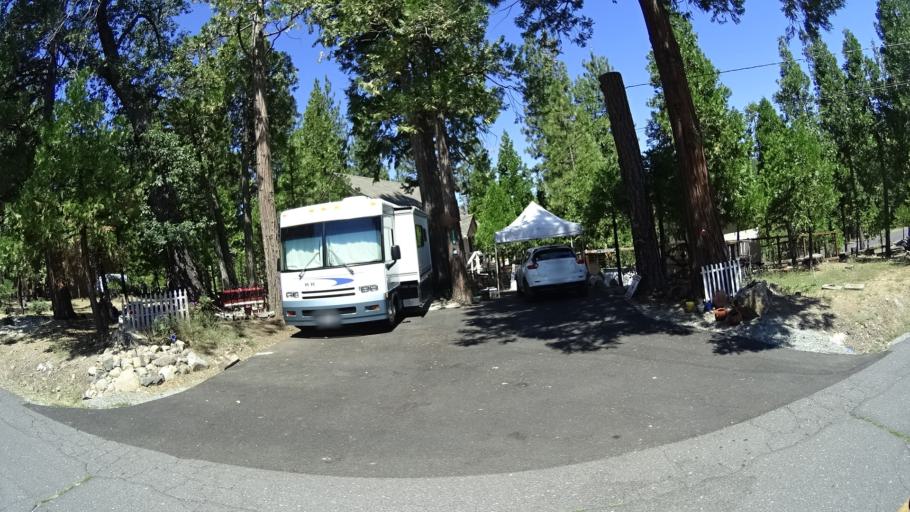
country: US
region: California
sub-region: Calaveras County
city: Arnold
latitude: 38.2332
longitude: -120.3698
